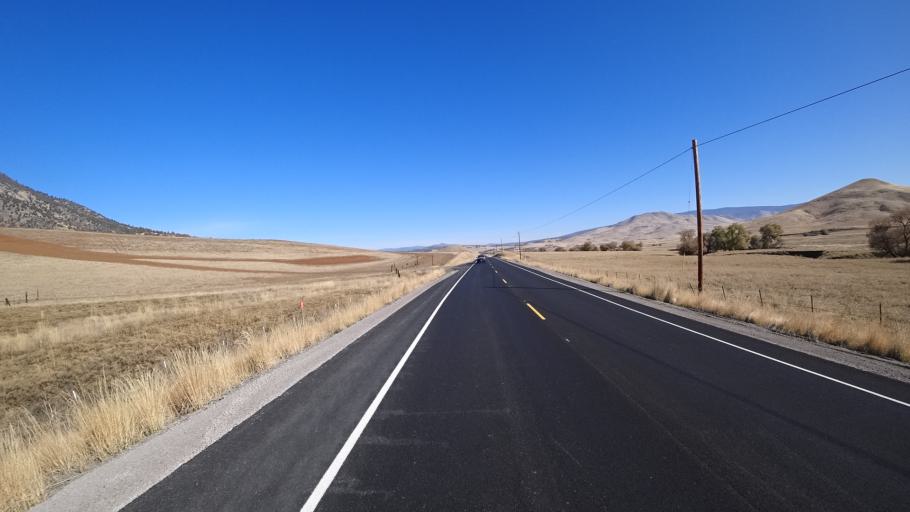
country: US
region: California
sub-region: Siskiyou County
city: Montague
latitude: 41.8296
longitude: -122.4924
